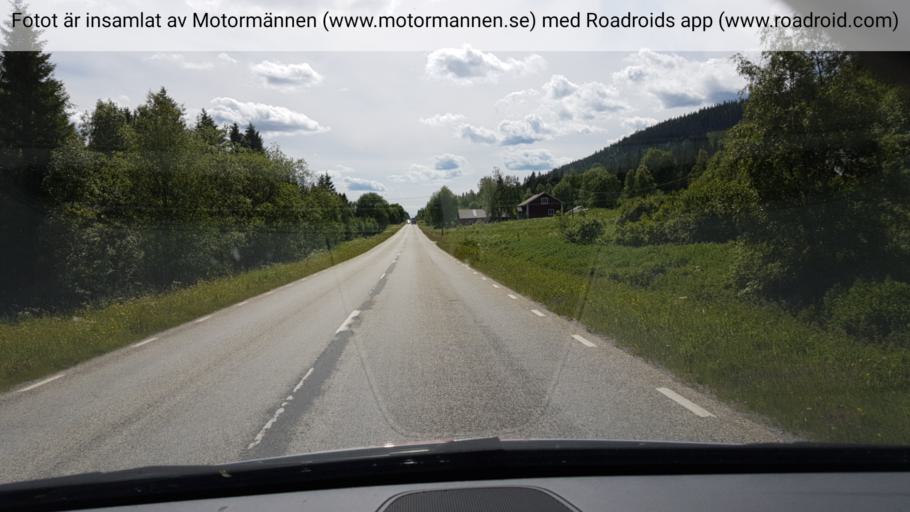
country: SE
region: Jaemtland
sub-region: Bergs Kommun
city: Hoverberg
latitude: 62.5831
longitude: 14.3086
